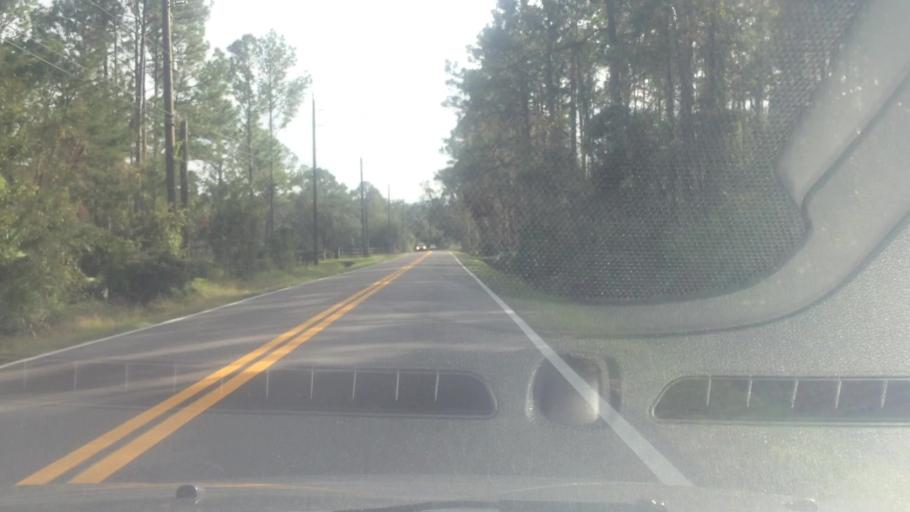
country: US
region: Florida
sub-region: Saint Johns County
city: Saint Augustine
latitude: 29.9237
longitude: -81.3612
